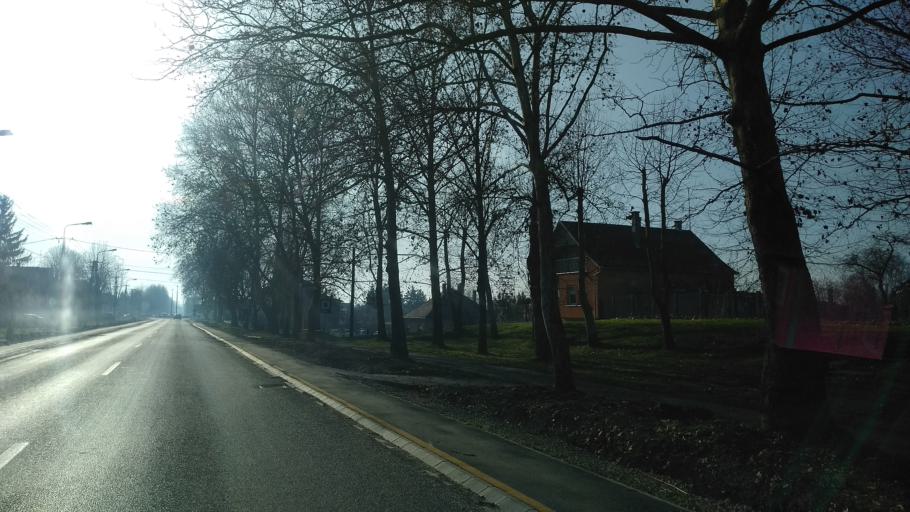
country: HU
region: Somogy
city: Barcs
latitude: 45.9683
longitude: 17.4589
